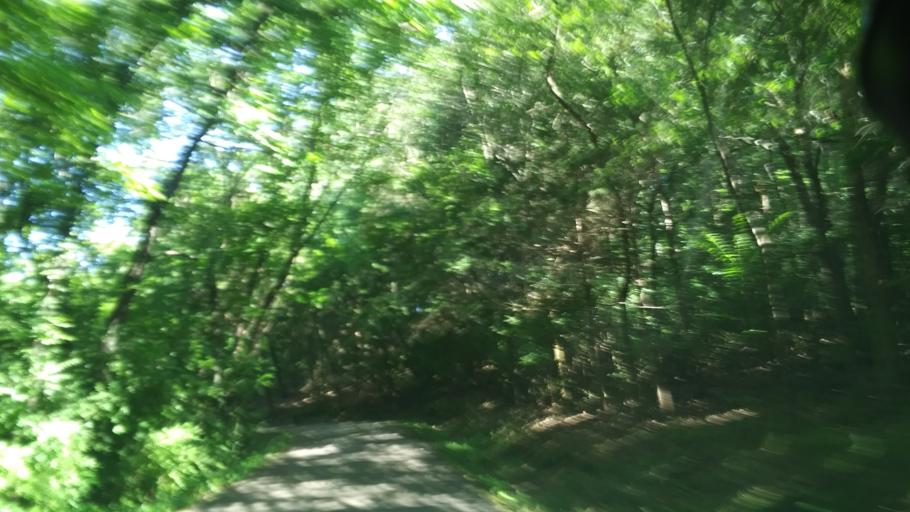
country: US
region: Tennessee
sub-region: Davidson County
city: Forest Hills
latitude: 36.0642
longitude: -86.8873
